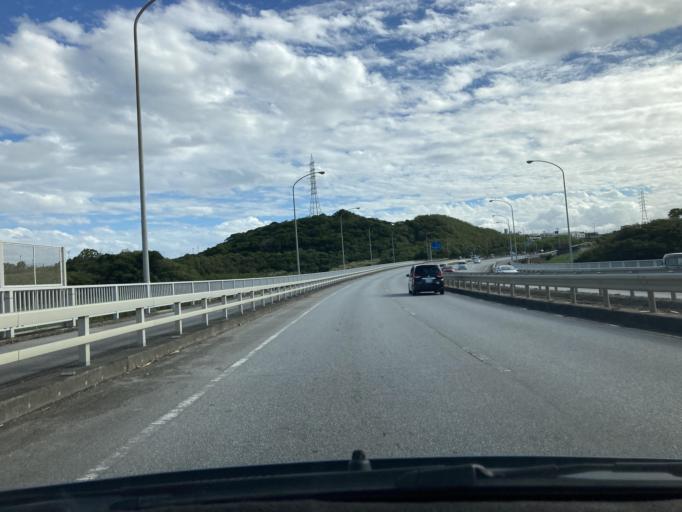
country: JP
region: Okinawa
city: Tomigusuku
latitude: 26.1778
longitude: 127.7267
